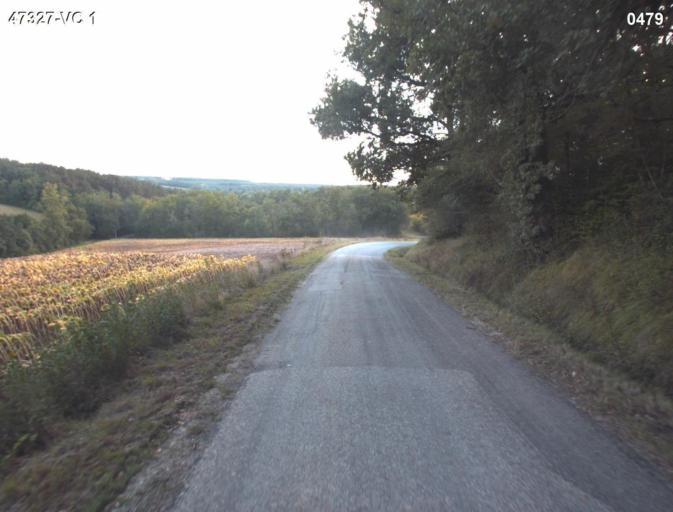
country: FR
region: Aquitaine
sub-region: Departement du Lot-et-Garonne
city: Barbaste
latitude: 44.1892
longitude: 0.2557
